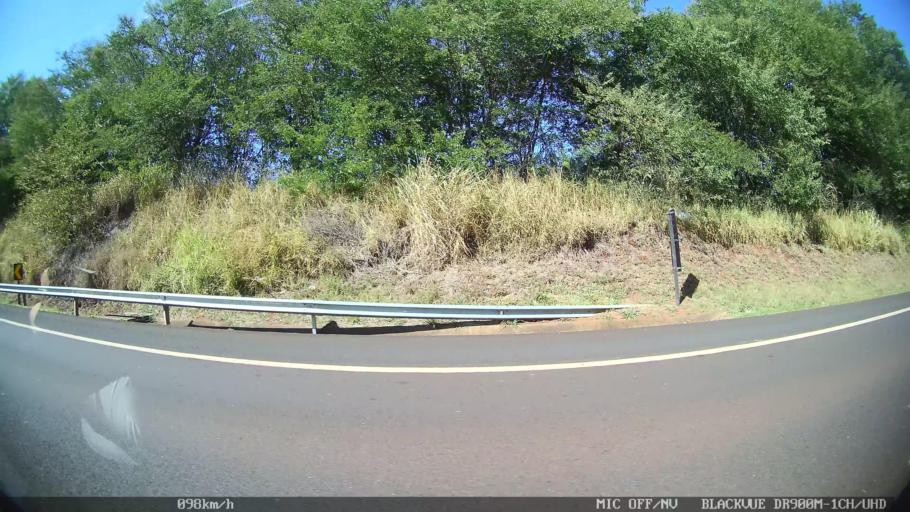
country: BR
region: Sao Paulo
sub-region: Franca
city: Franca
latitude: -20.5830
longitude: -47.4298
